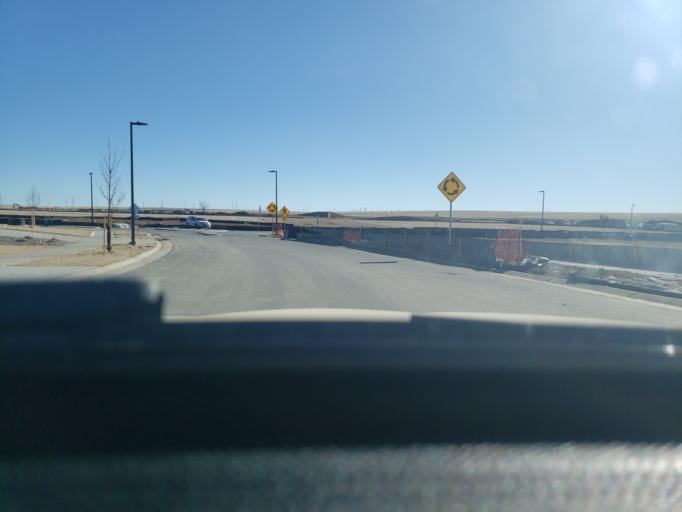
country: US
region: Colorado
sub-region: Adams County
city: Aurora
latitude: 39.7714
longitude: -104.7032
